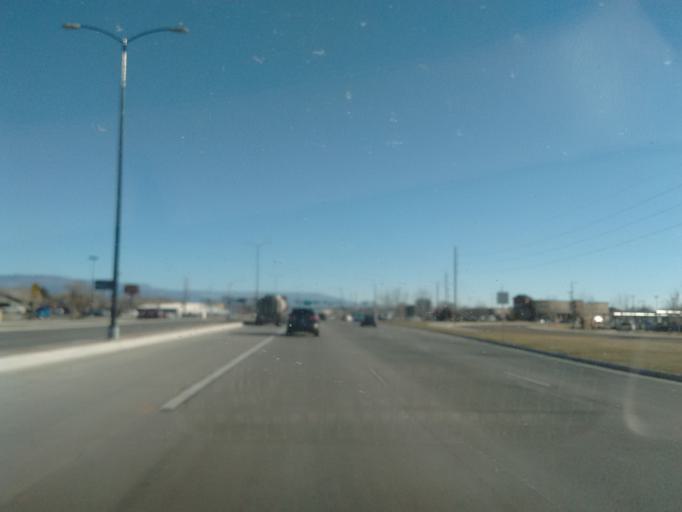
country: US
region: Colorado
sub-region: Mesa County
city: Grand Junction
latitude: 39.0814
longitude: -108.5856
